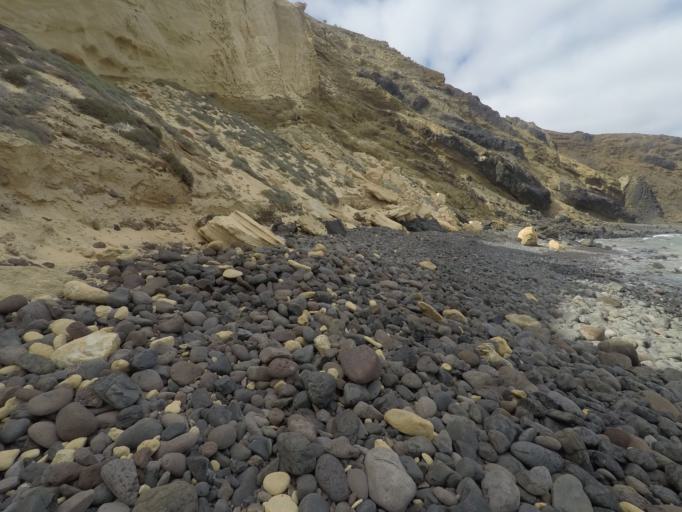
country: PT
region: Madeira
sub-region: Porto Santo
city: Vila de Porto Santo
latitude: 33.0744
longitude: -16.2950
